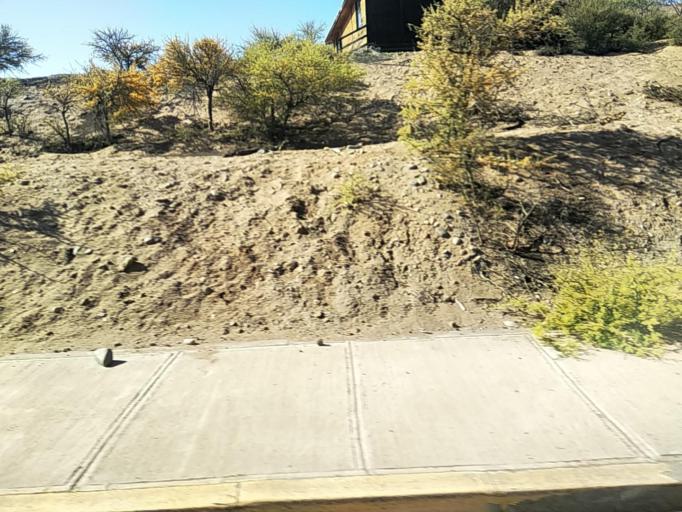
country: CL
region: Atacama
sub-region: Provincia de Copiapo
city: Copiapo
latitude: -27.3351
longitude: -70.7786
